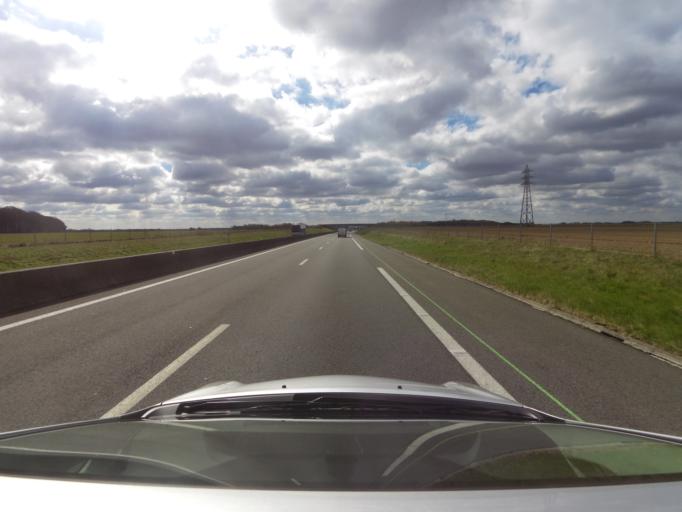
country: FR
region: Picardie
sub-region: Departement de la Somme
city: Rue
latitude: 50.2906
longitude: 1.7306
